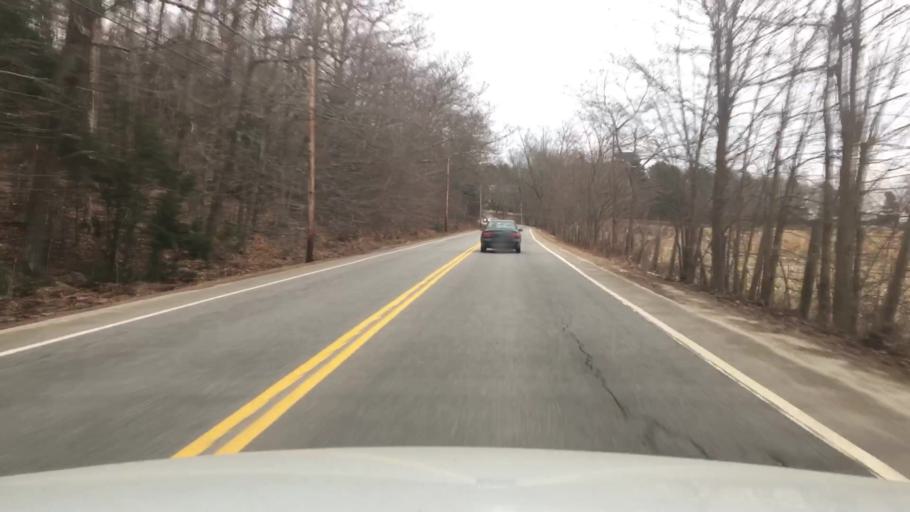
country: US
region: Maine
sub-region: Cumberland County
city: Freeport
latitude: 43.8811
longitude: -70.0392
